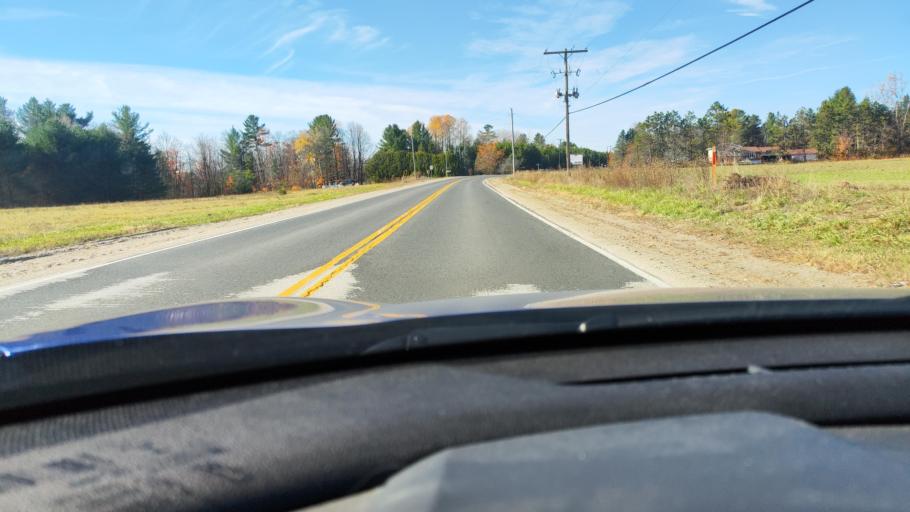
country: CA
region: Ontario
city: Angus
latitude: 44.3430
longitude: -80.0195
